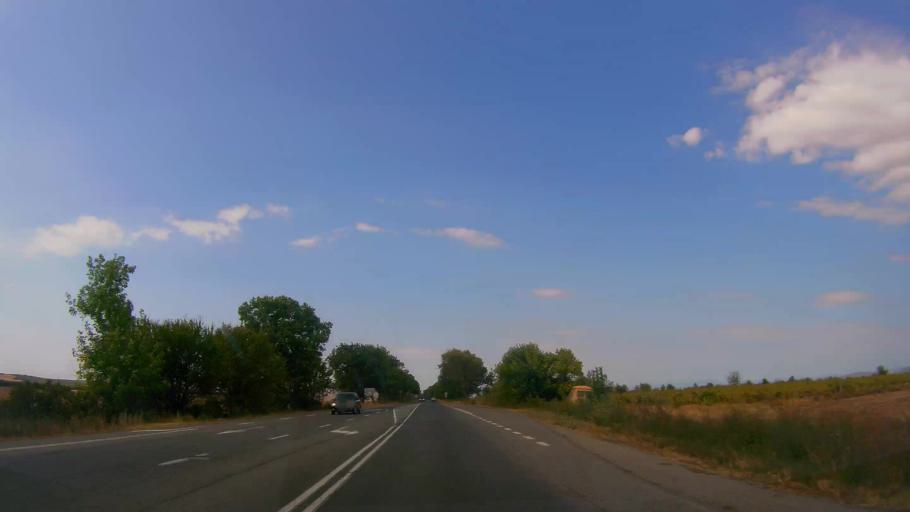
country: BG
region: Burgas
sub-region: Obshtina Karnobat
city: Karnobat
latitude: 42.6796
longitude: 27.1143
